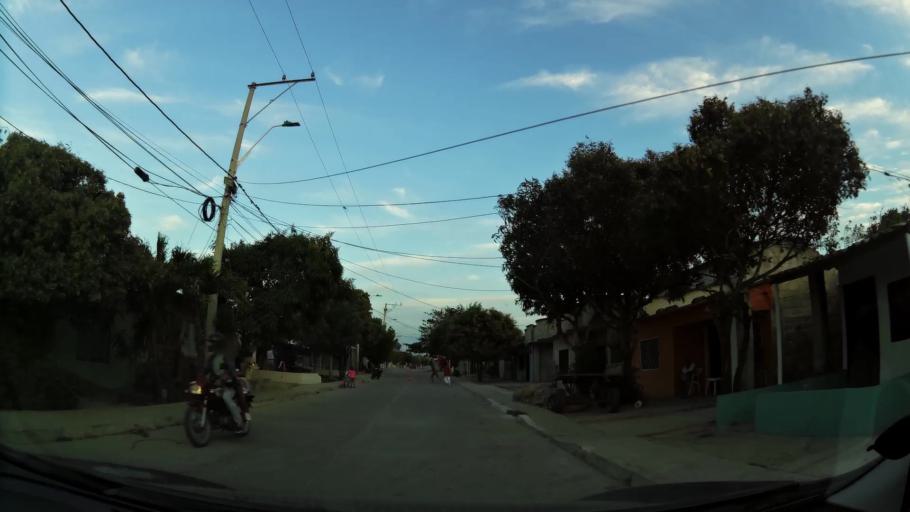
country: CO
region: Atlantico
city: Barranquilla
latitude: 10.9602
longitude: -74.8232
